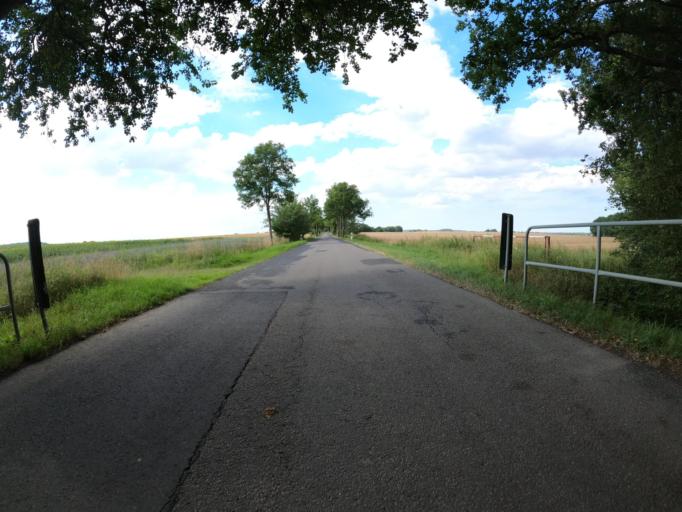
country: DE
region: Mecklenburg-Vorpommern
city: Woldegk
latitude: 53.4317
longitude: 13.6010
